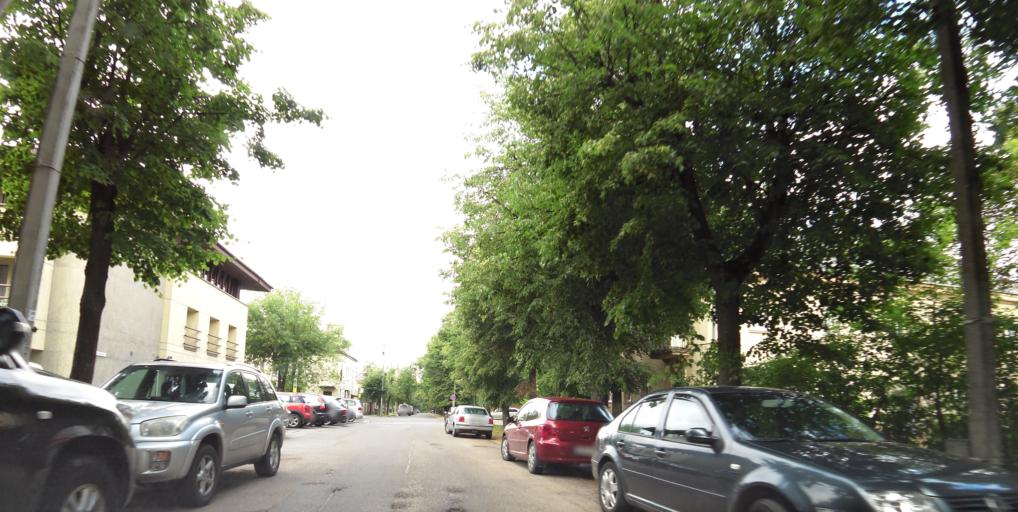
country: LT
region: Vilnius County
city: Seskine
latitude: 54.6909
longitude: 25.2525
